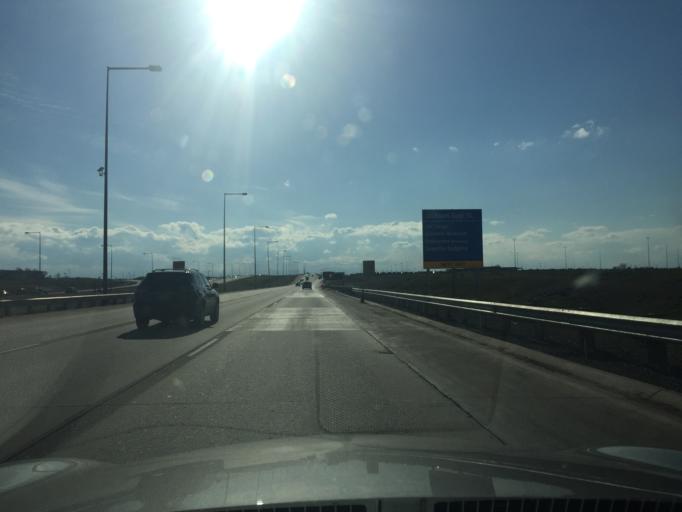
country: US
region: Colorado
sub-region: Weld County
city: Lochbuie
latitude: 39.8342
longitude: -104.6815
